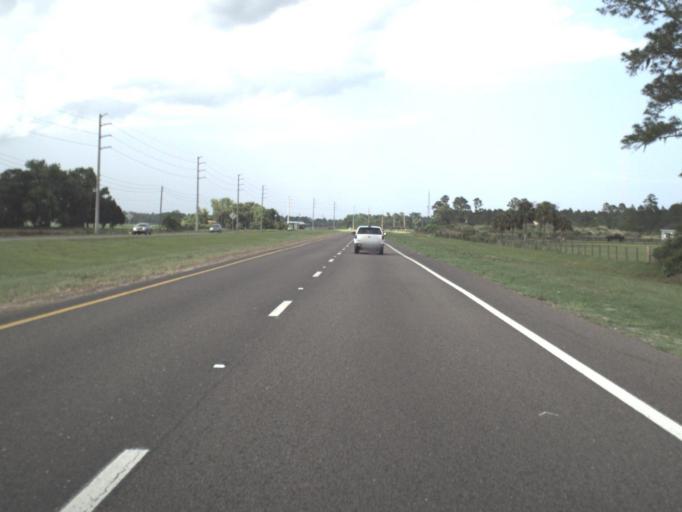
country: US
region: Florida
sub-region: Putnam County
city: East Palatka
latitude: 29.7469
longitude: -81.4702
